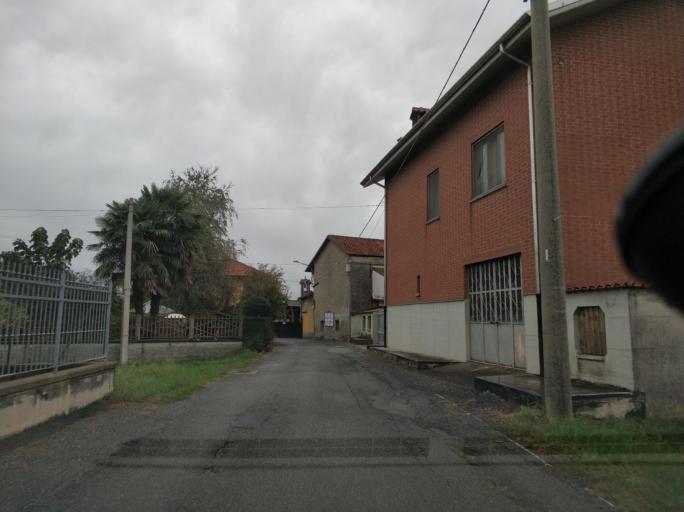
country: IT
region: Piedmont
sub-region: Provincia di Torino
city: Cirie
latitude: 45.2161
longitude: 7.6014
